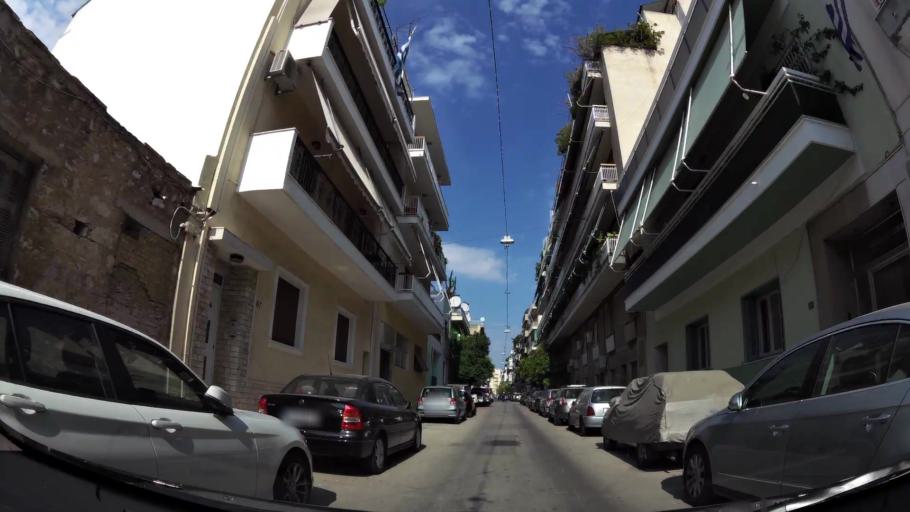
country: GR
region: Attica
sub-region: Nomarchia Athinas
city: Kipseli
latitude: 38.0095
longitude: 23.7269
